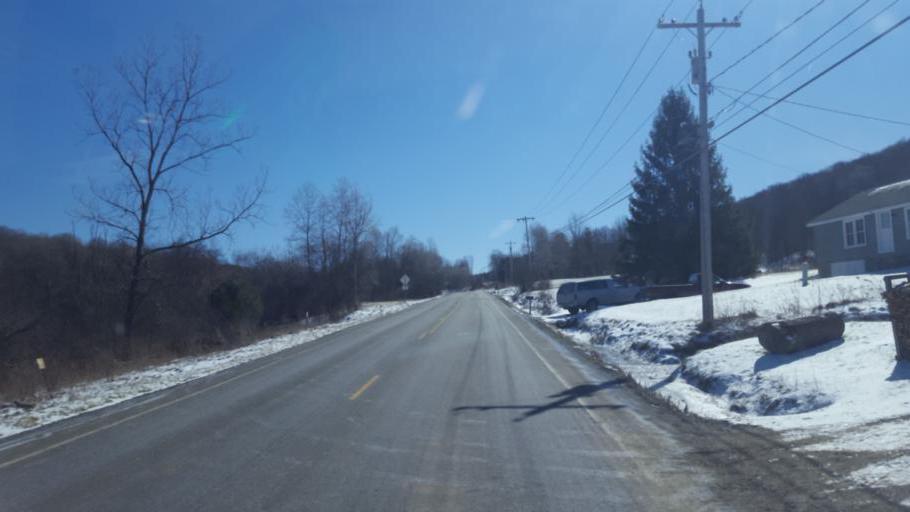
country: US
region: New York
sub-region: Allegany County
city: Andover
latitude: 42.0733
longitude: -77.8485
